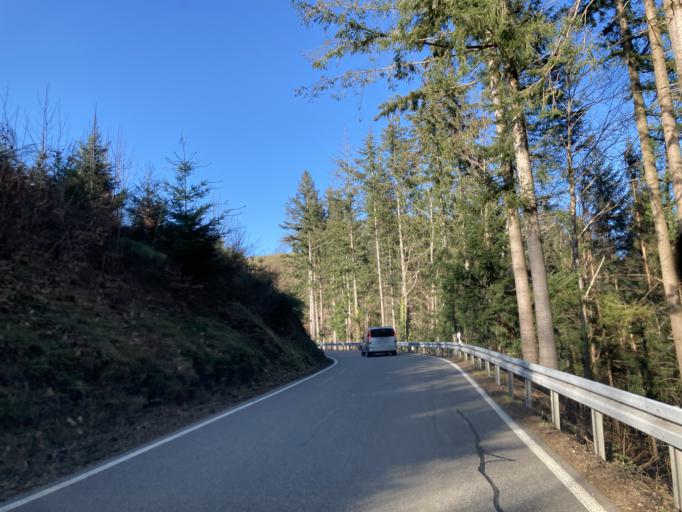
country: DE
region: Baden-Wuerttemberg
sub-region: Freiburg Region
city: Oppenau
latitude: 48.4793
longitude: 8.2029
